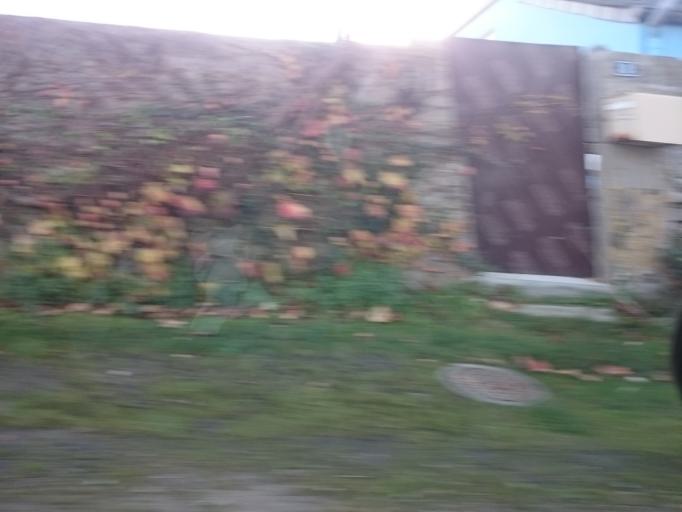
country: FR
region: Brittany
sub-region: Departement du Finistere
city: Landunvez
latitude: 48.5302
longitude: -4.7472
